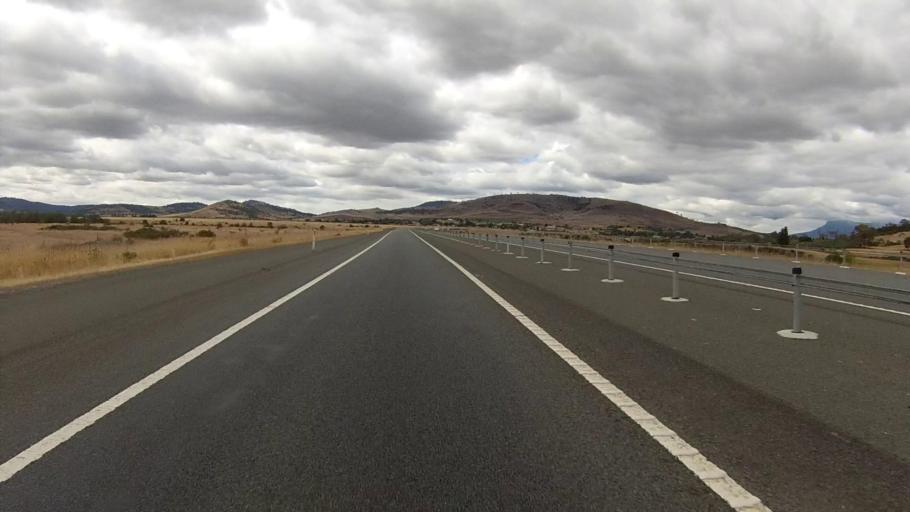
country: AU
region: Tasmania
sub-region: Brighton
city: Bridgewater
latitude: -42.6790
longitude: 147.2728
